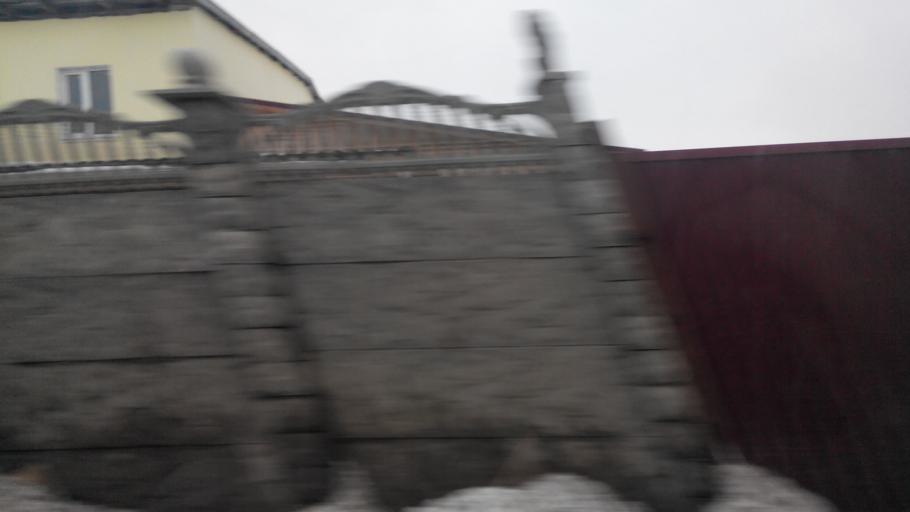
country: RU
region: Tula
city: Mayskiy
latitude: 53.9796
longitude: 38.2279
